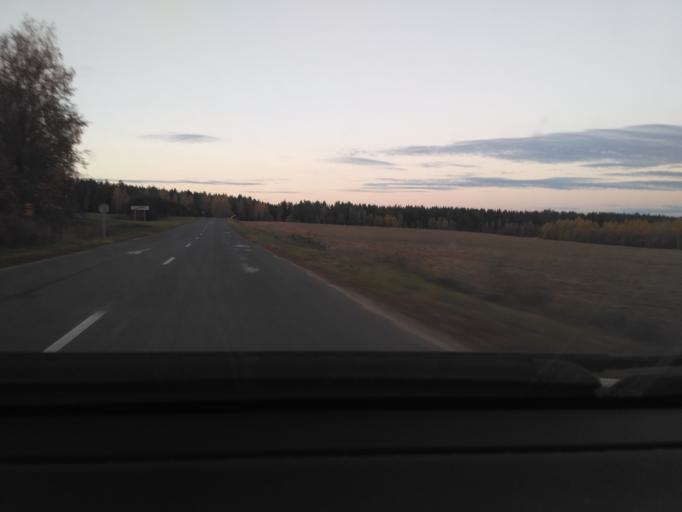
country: BY
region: Minsk
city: Loshnitsa
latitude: 54.3666
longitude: 28.6236
